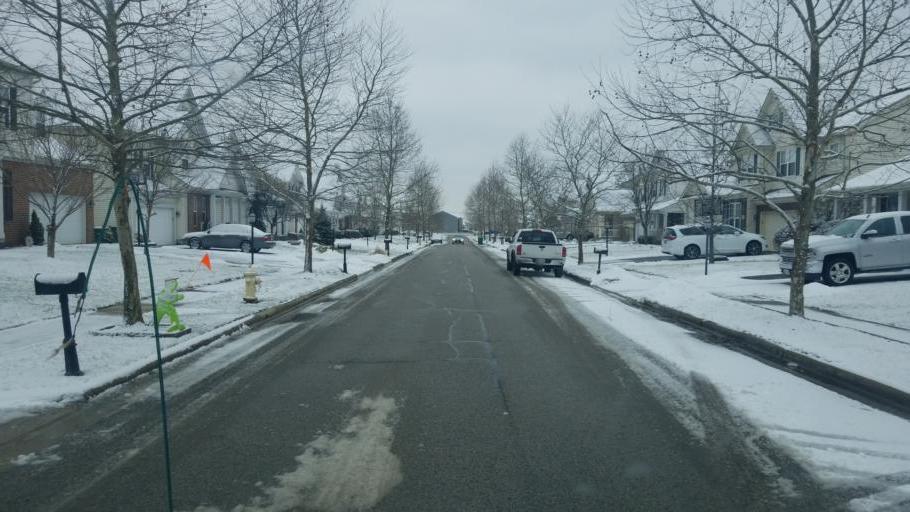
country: US
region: Ohio
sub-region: Franklin County
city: Reynoldsburg
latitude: 40.0167
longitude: -82.7946
